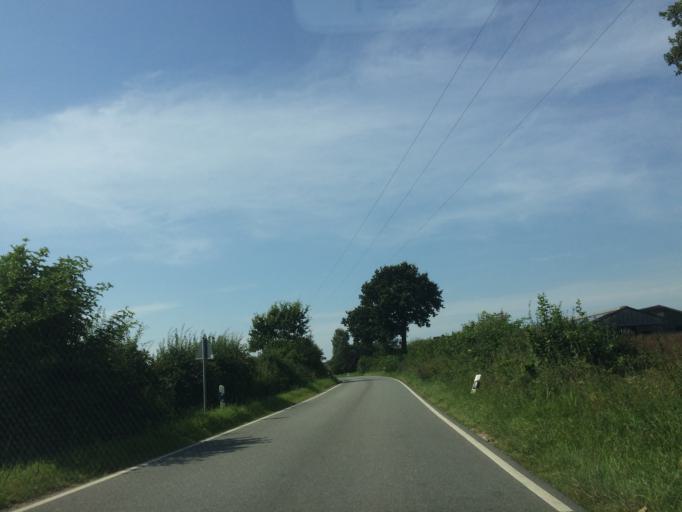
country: DE
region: Schleswig-Holstein
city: Altenhof
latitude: 54.4113
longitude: 9.8776
